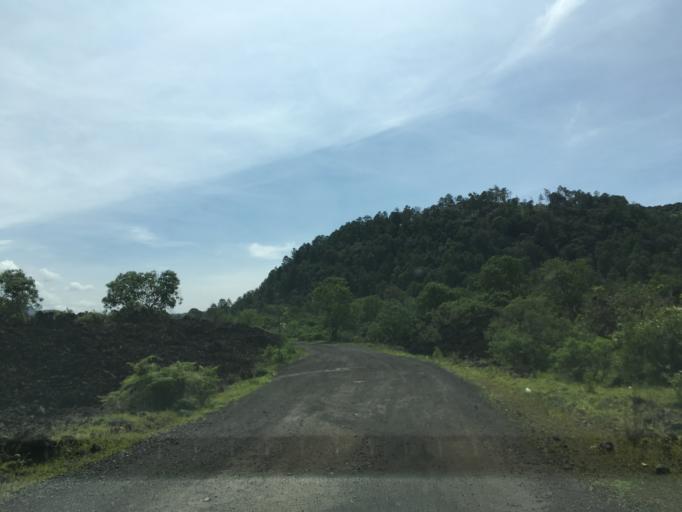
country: MX
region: Michoacan
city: Angahuan
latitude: 19.5273
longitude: -102.2462
